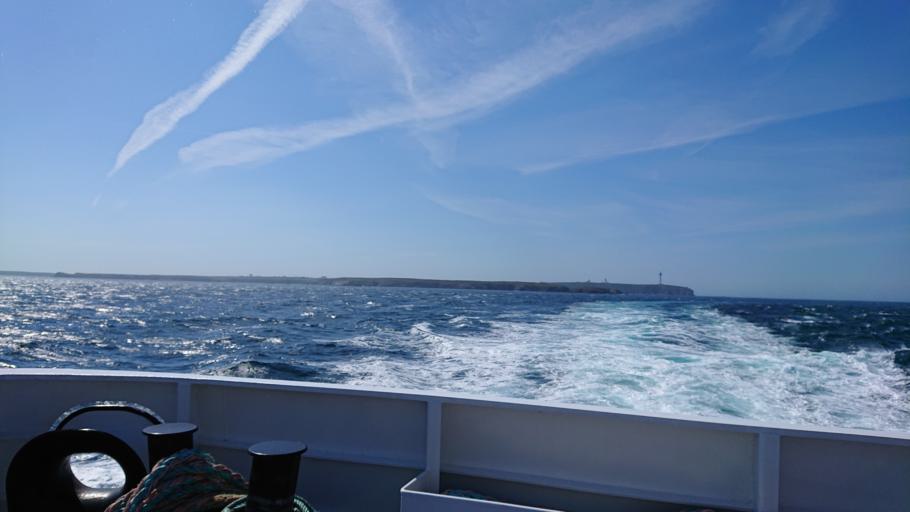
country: FR
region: Brittany
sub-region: Departement du Finistere
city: Porspoder
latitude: 48.4549
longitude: -5.0141
